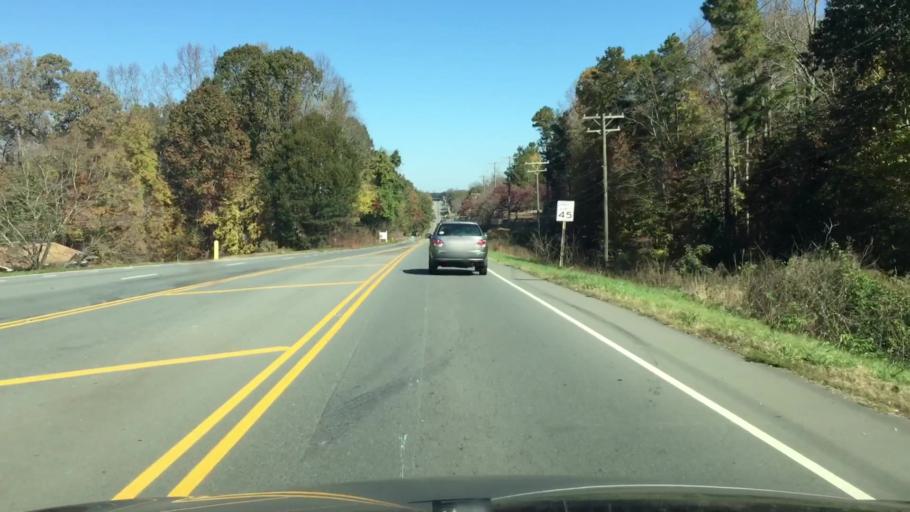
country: US
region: North Carolina
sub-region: Iredell County
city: Mooresville
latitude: 35.5620
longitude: -80.8497
